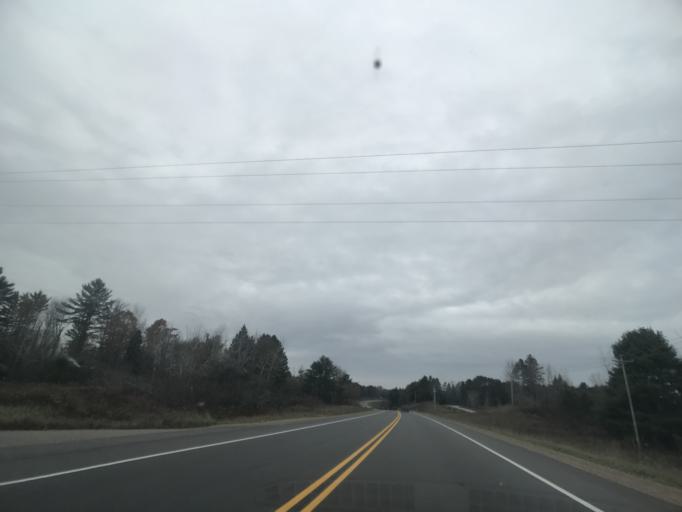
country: US
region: Wisconsin
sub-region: Menominee County
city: Legend Lake
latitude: 45.1970
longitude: -88.4943
